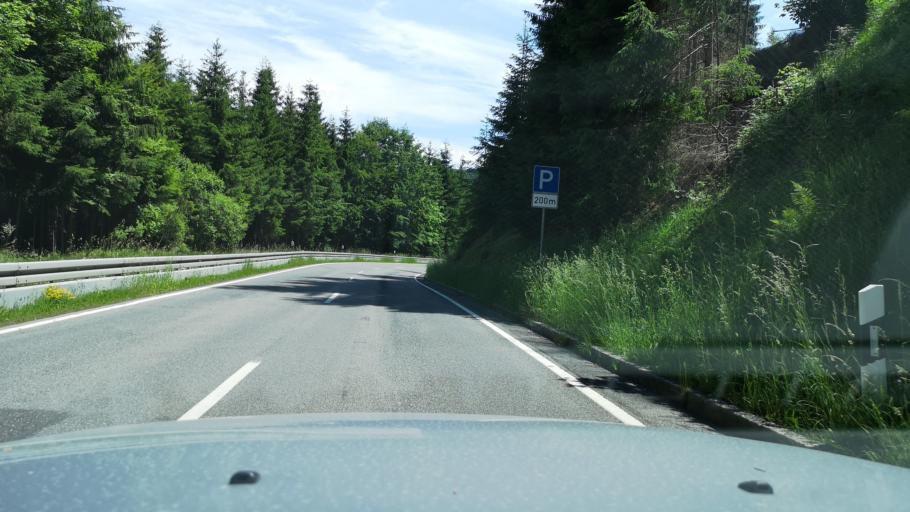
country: DE
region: Bavaria
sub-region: Upper Franconia
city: Tschirn
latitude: 50.3992
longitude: 11.4800
